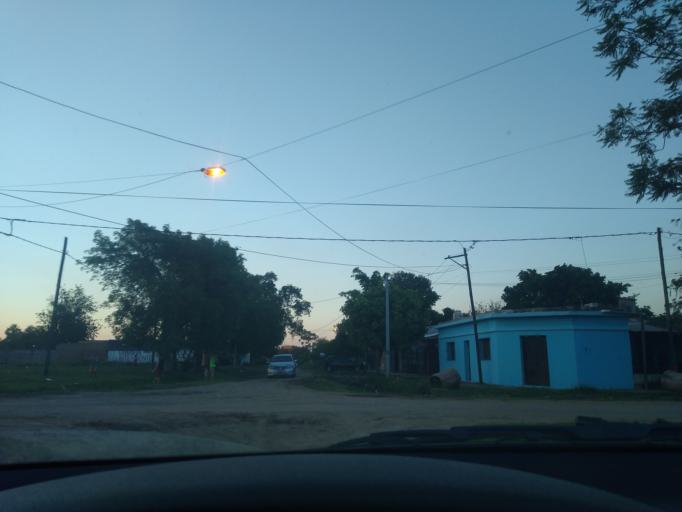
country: AR
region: Chaco
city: Barranqueras
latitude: -27.4766
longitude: -58.9341
